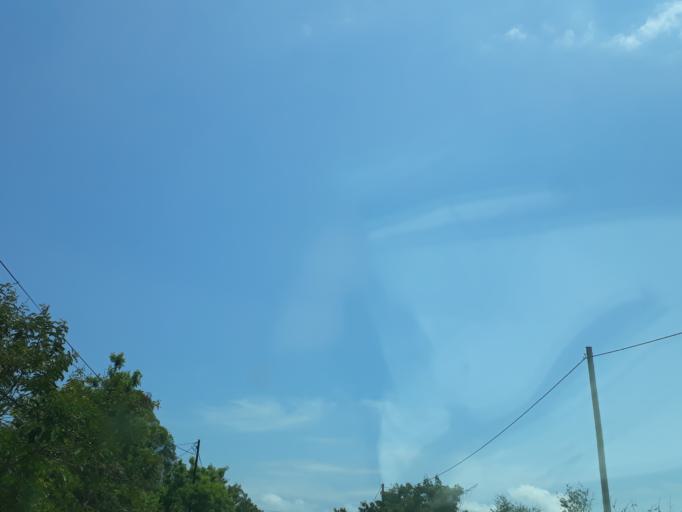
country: TZ
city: Kiwengwa
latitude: -5.9909
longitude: 39.3732
